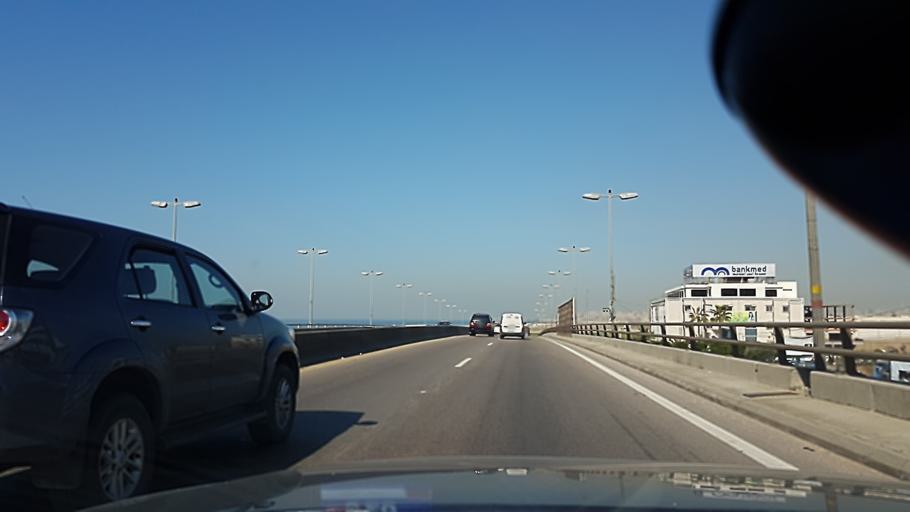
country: LB
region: Mont-Liban
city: Baabda
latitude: 33.7950
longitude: 35.4829
